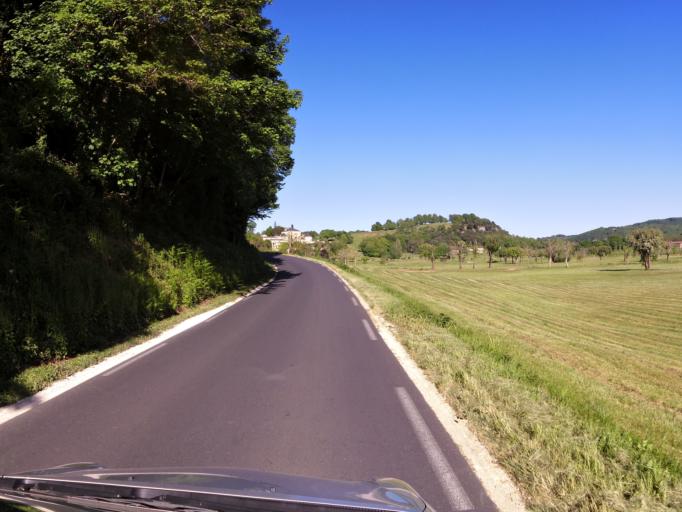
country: FR
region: Aquitaine
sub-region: Departement de la Dordogne
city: Carsac-Aillac
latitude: 44.8302
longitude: 1.2317
